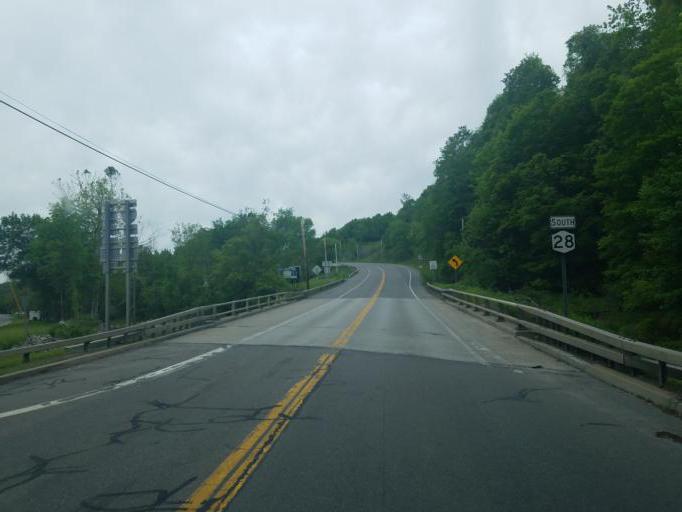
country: US
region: New York
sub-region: Herkimer County
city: Mohawk
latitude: 43.0022
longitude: -75.0077
